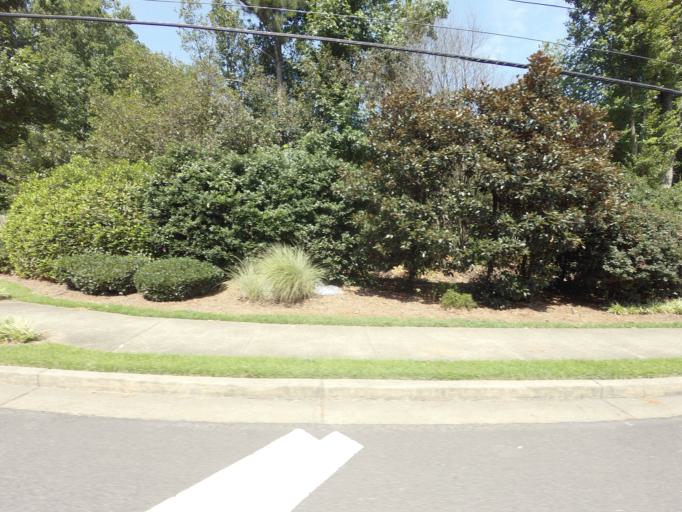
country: US
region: Georgia
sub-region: Fulton County
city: Alpharetta
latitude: 34.0256
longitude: -84.2695
